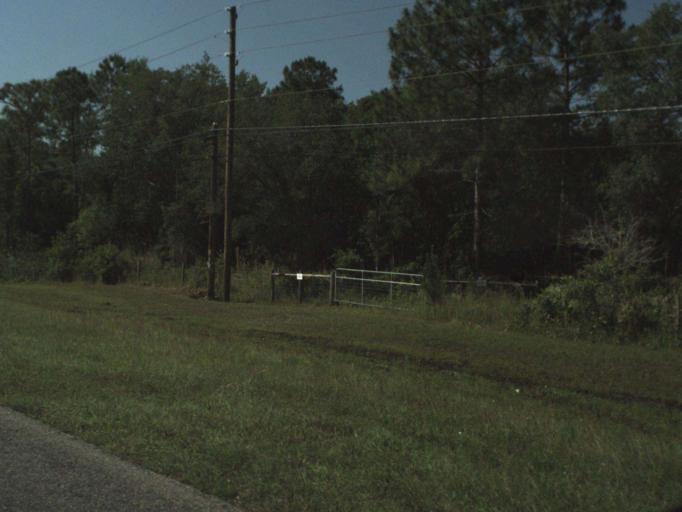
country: US
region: Florida
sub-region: Orange County
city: Bithlo
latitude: 28.5329
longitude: -81.0776
